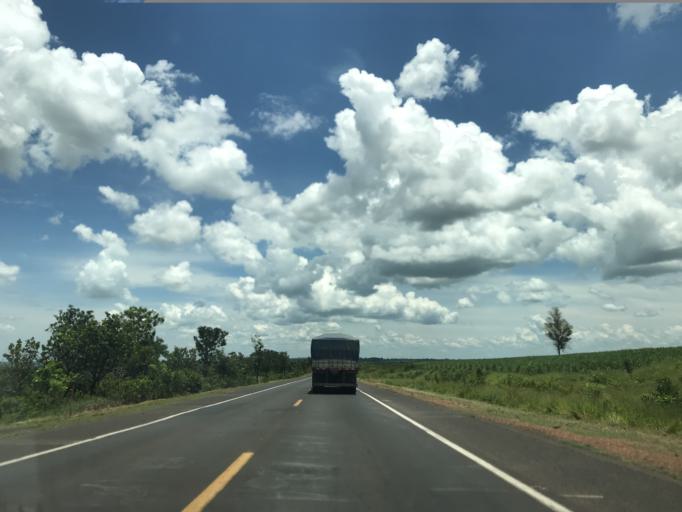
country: BR
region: Minas Gerais
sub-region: Prata
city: Prata
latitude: -19.5390
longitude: -48.8297
